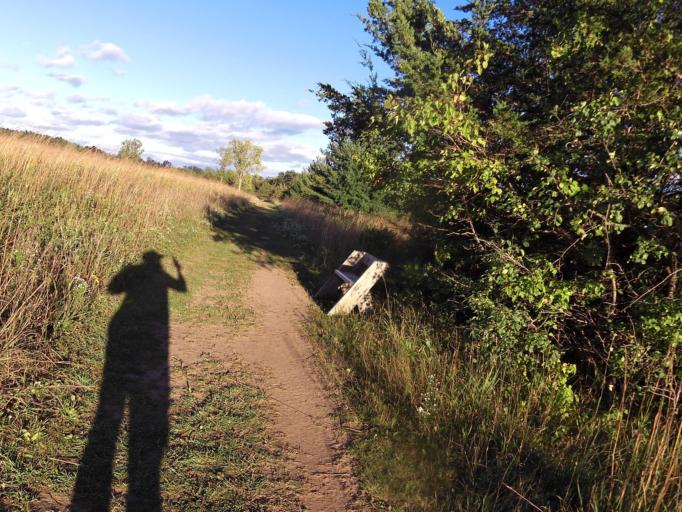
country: US
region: Minnesota
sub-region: Washington County
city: Lake Saint Croix Beach
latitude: 44.9313
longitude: -92.7901
